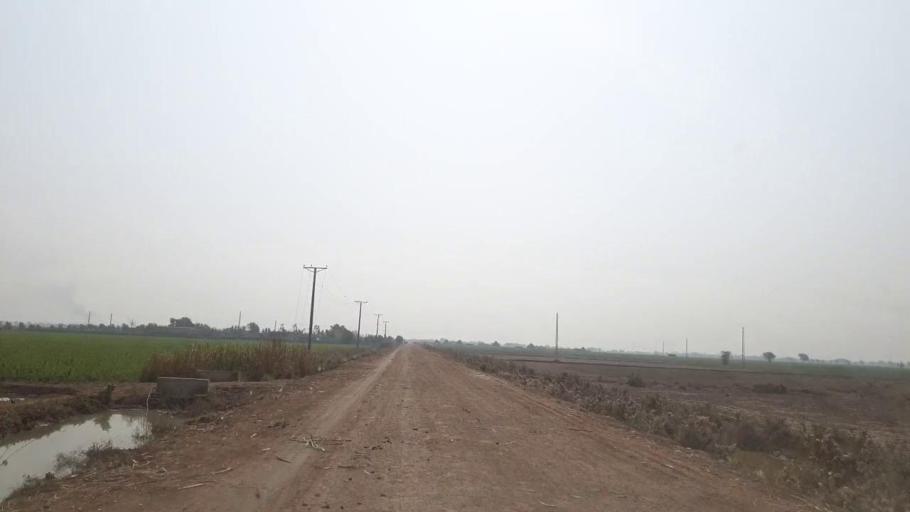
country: PK
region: Sindh
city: Mirpur Khas
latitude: 25.5461
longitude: 69.0596
